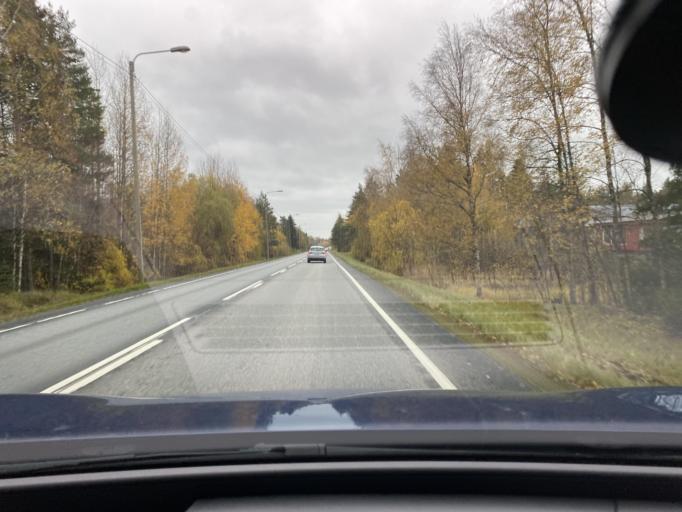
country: FI
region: Varsinais-Suomi
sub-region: Vakka-Suomi
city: Pyhaeranta
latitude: 60.9940
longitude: 21.5778
